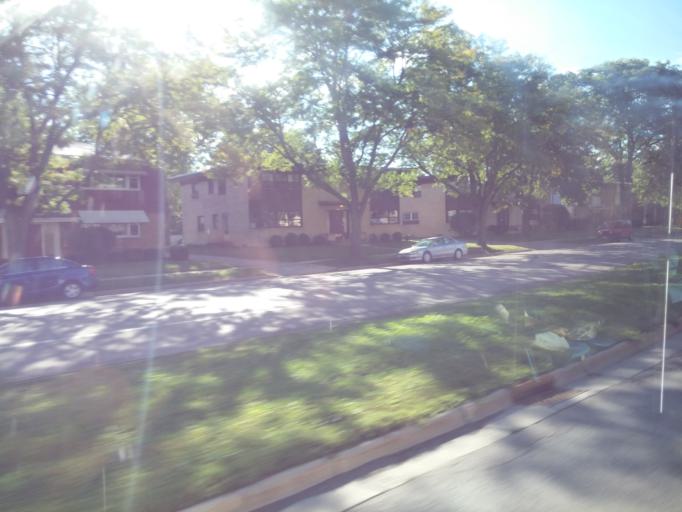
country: US
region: Wisconsin
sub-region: Dane County
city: Shorewood Hills
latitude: 43.0722
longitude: -89.4512
